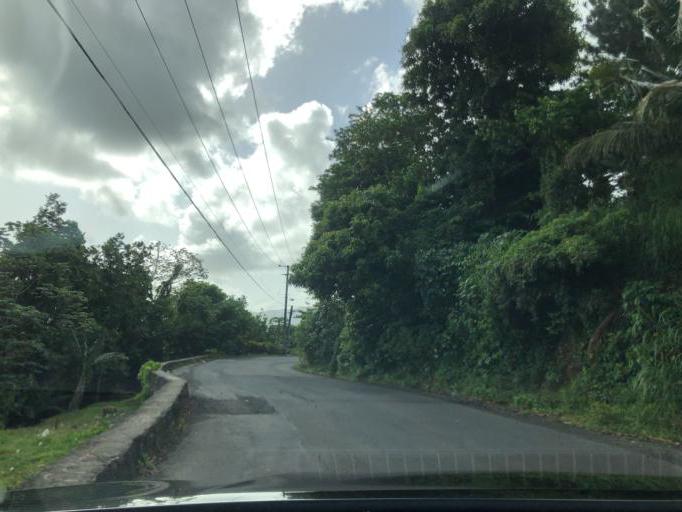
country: LC
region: Castries Quarter
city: Bisee
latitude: 14.0006
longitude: -60.9492
